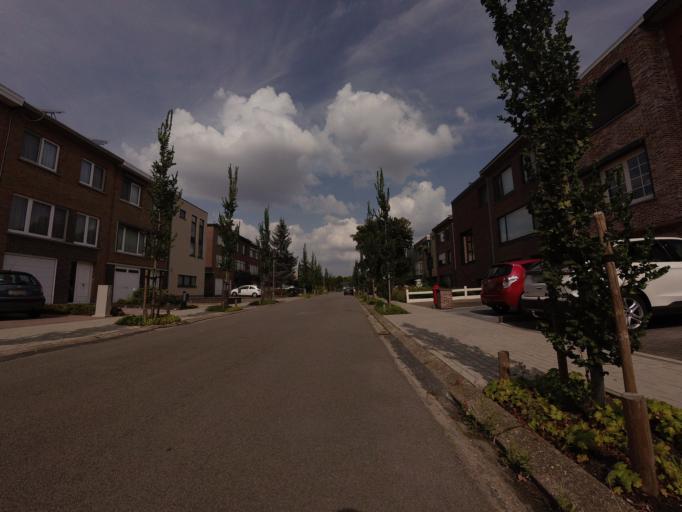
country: BE
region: Flanders
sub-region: Provincie Antwerpen
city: Aartselaar
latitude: 51.1383
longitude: 4.3855
